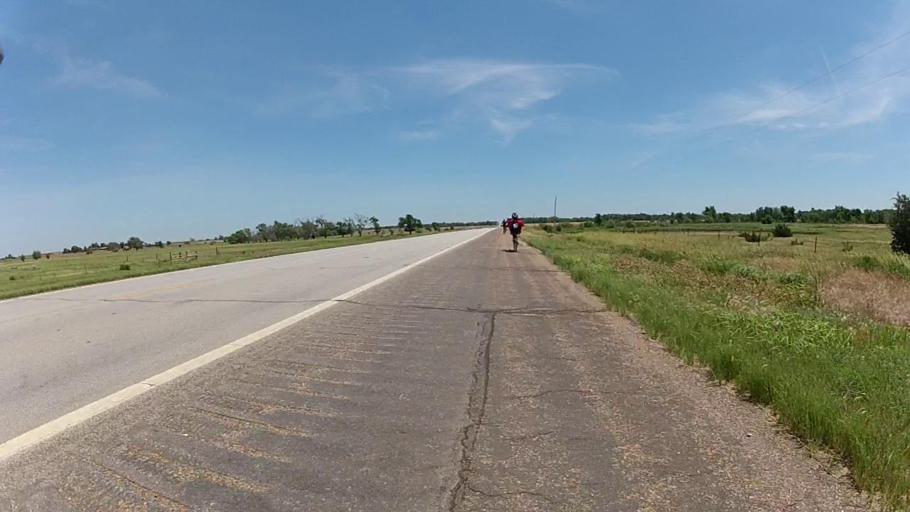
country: US
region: Kansas
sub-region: Barber County
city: Medicine Lodge
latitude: 37.2533
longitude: -98.3176
